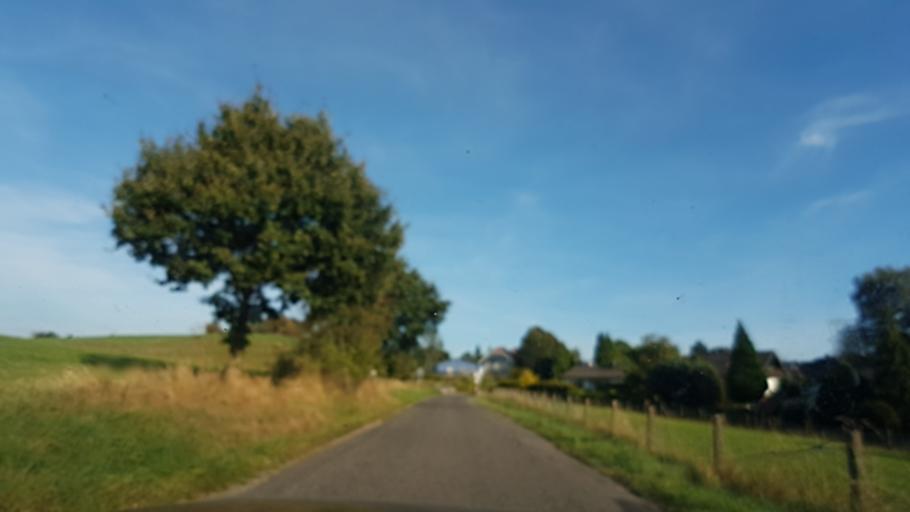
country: DE
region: North Rhine-Westphalia
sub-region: Regierungsbezirk Koln
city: Marienheide
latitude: 51.1153
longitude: 7.5016
